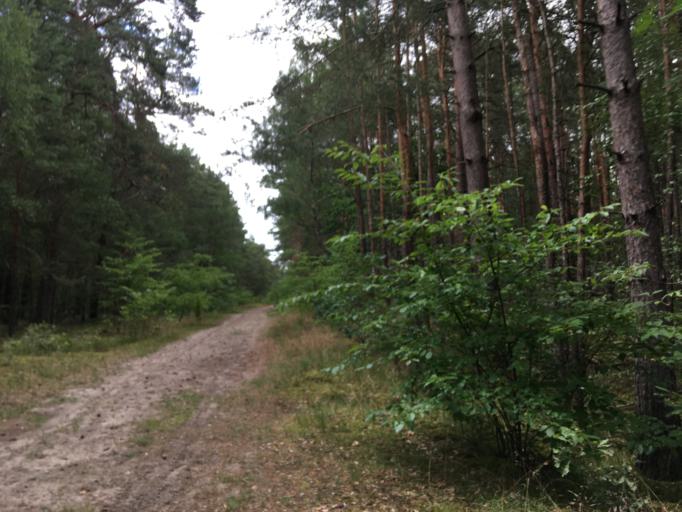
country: DE
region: Brandenburg
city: Bernau bei Berlin
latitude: 52.6897
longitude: 13.5279
